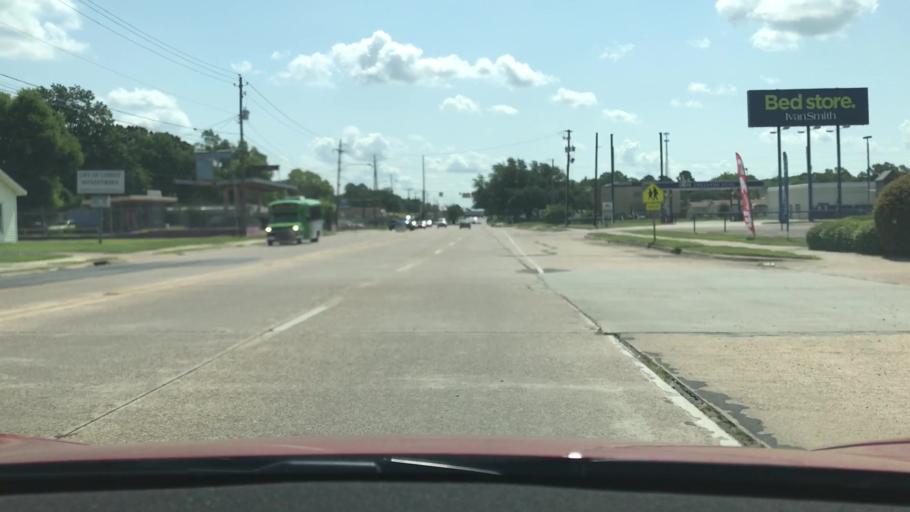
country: US
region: Louisiana
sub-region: Bossier Parish
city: Bossier City
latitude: 32.4420
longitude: -93.7669
